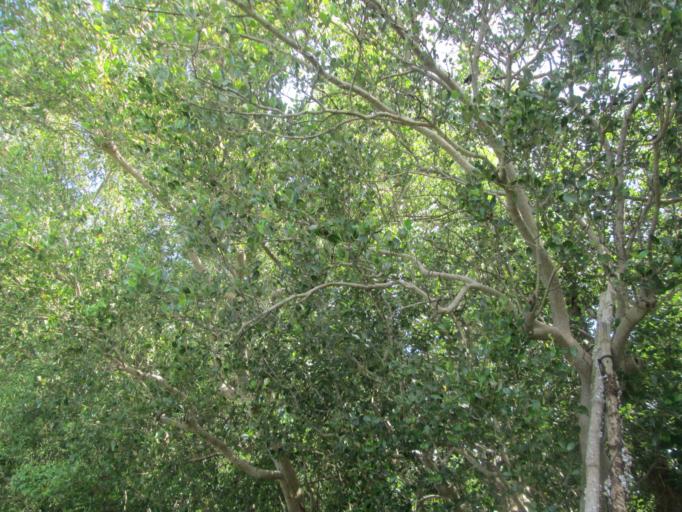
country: PH
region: Ilocos
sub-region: Province of Pangasinan
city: Pangapisan
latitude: 16.2428
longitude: 119.9296
